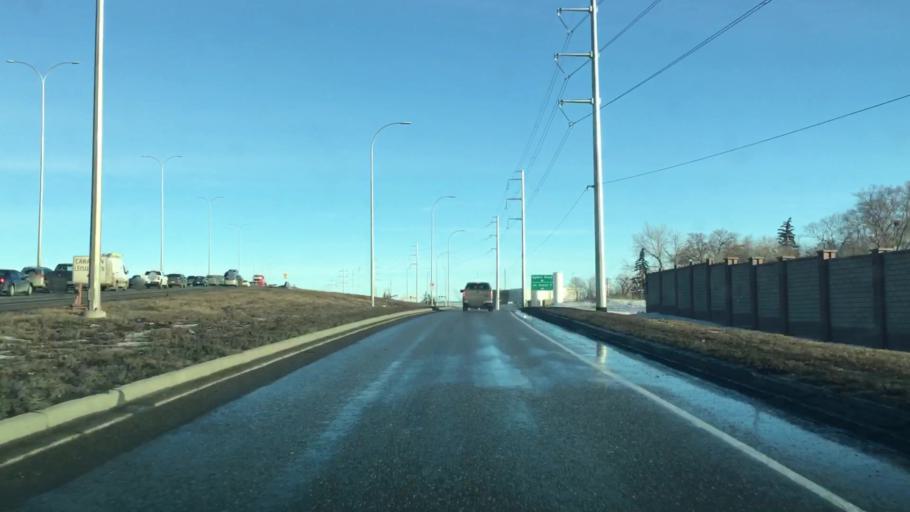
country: CA
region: Alberta
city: Calgary
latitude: 50.9789
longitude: -114.0029
